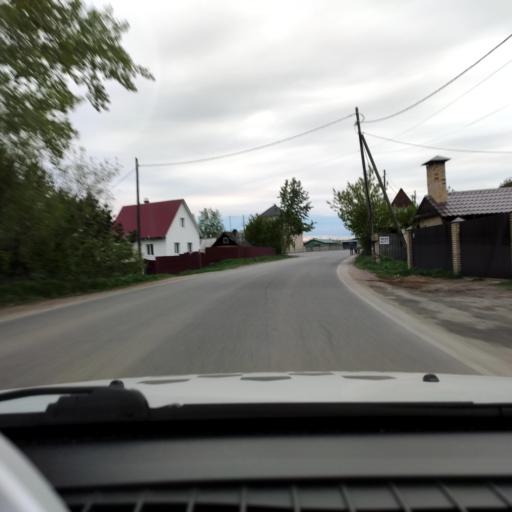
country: RU
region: Perm
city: Kondratovo
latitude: 58.0131
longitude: 56.0431
